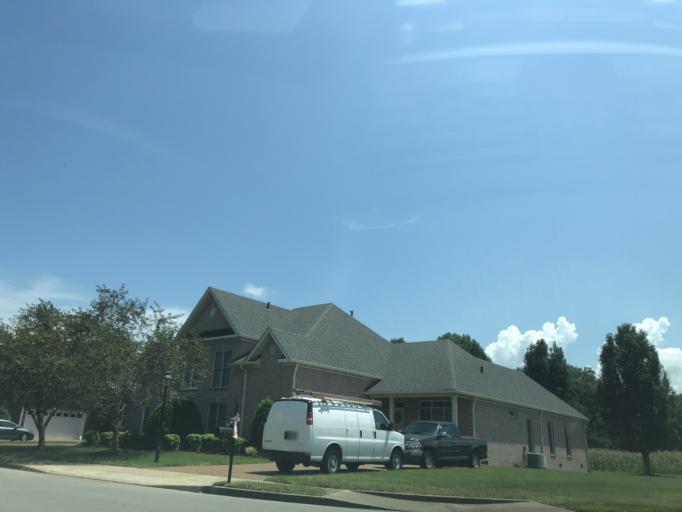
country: US
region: Tennessee
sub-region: Davidson County
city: Lakewood
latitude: 36.1957
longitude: -86.6026
